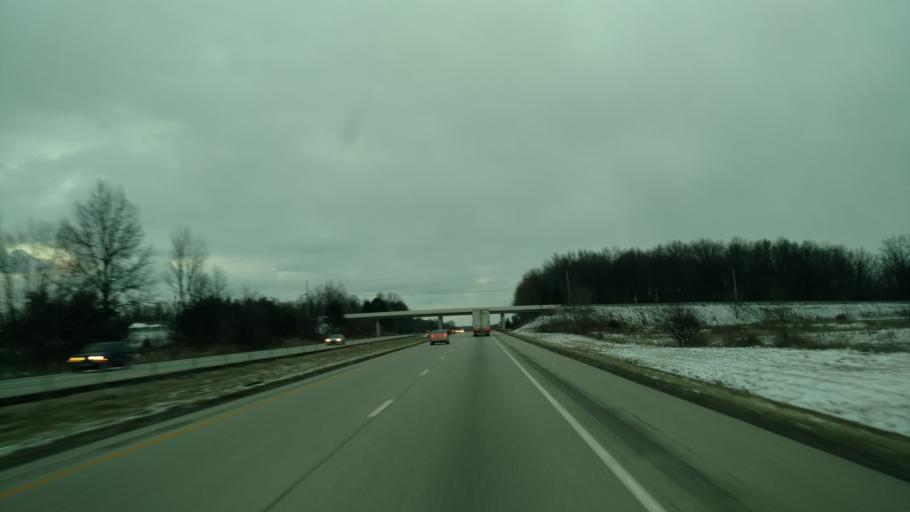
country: US
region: Ohio
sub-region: Medina County
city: Seville
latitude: 41.0319
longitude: -81.8125
